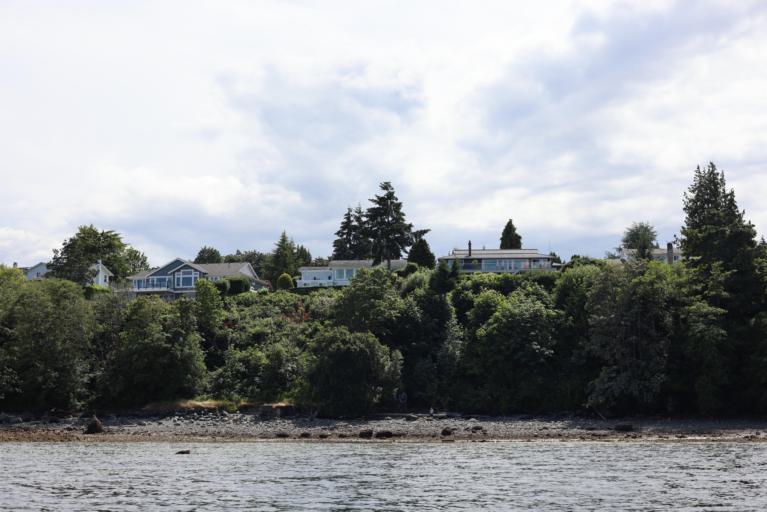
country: CA
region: British Columbia
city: Nanaimo
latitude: 49.1963
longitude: -123.9601
